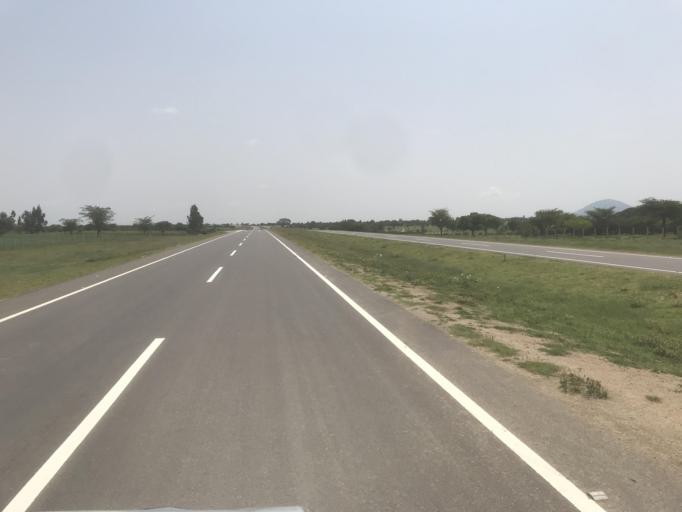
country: ET
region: Oromiya
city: Ziway
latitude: 8.2528
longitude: 38.8912
